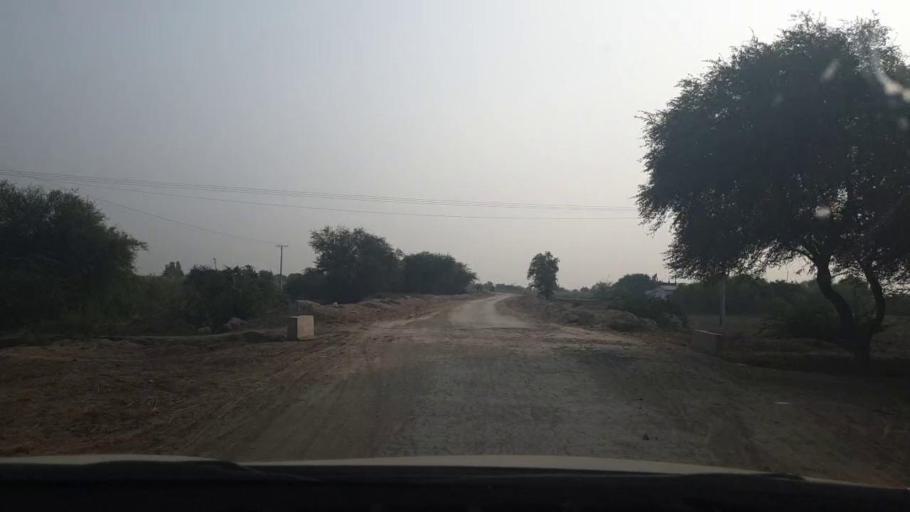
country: PK
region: Sindh
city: Bulri
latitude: 24.7886
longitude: 68.4258
